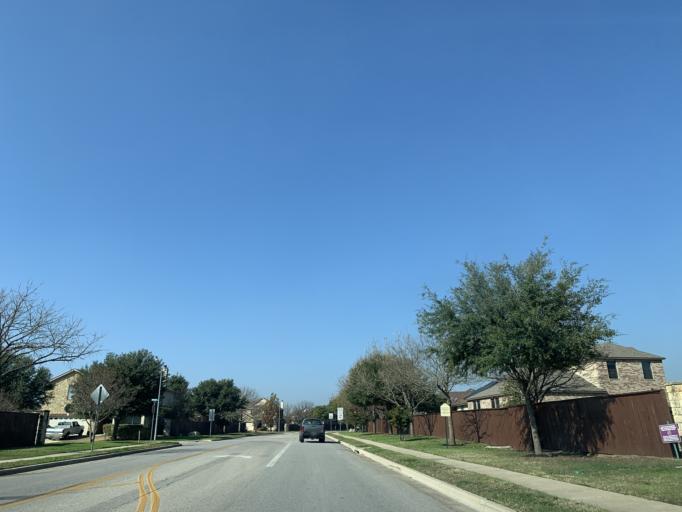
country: US
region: Texas
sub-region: Williamson County
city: Round Rock
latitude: 30.5288
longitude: -97.6404
